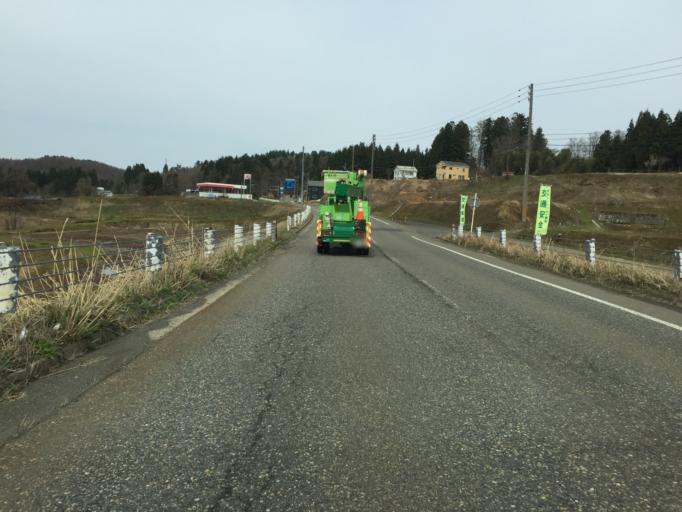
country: JP
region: Niigata
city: Tochio-honcho
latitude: 37.4559
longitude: 138.9687
